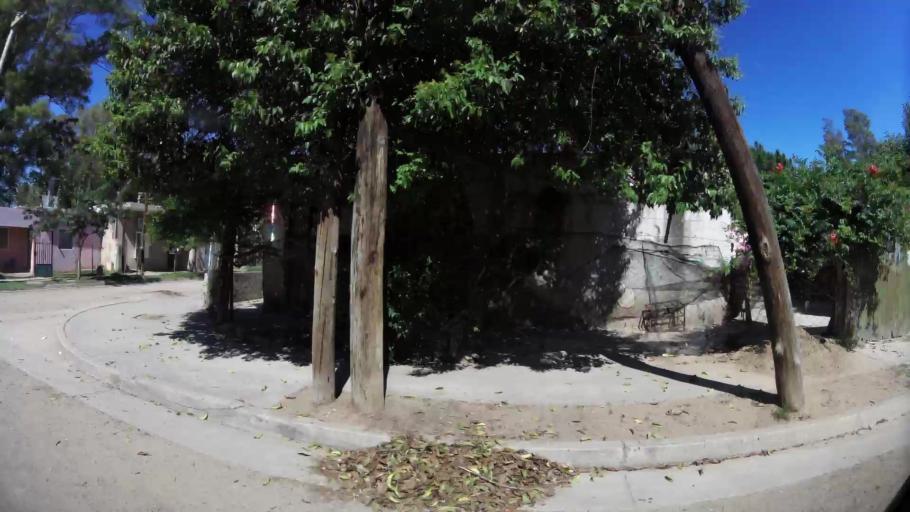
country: AR
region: Cordoba
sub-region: Departamento de Capital
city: Cordoba
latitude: -31.4392
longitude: -64.1316
